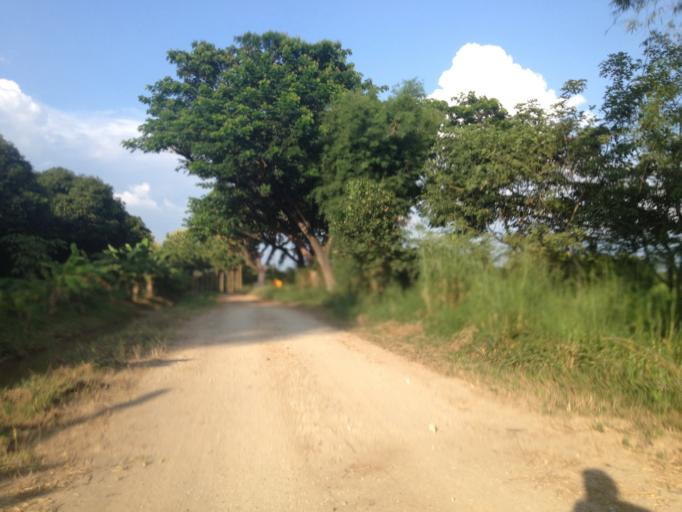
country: TH
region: Chiang Mai
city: Hang Dong
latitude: 18.6945
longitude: 98.8999
